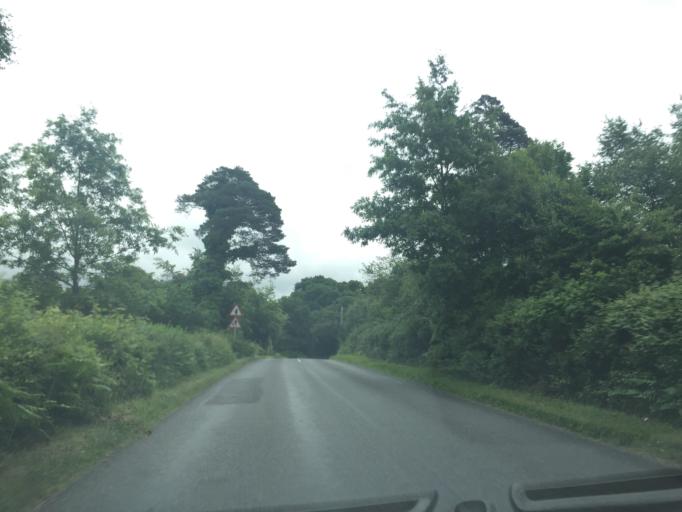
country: GB
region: England
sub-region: Dorset
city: Bovington Camp
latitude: 50.7200
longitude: -2.2590
